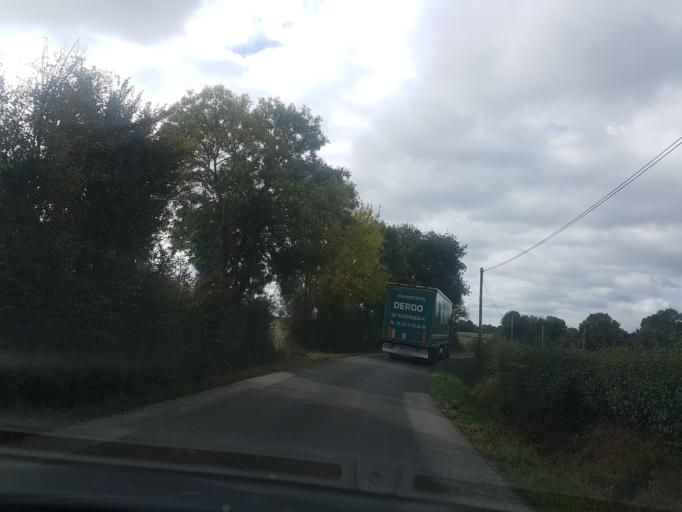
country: FR
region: Pays de la Loire
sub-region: Departement de la Loire-Atlantique
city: Ligne
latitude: 47.3992
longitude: -1.3964
